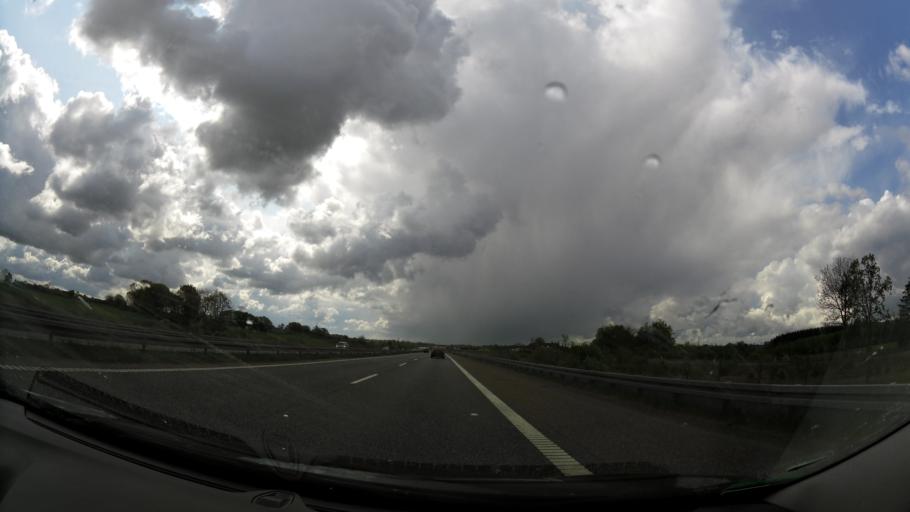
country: DK
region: South Denmark
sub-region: Faaborg-Midtfyn Kommune
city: Ringe
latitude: 55.1965
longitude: 10.5195
